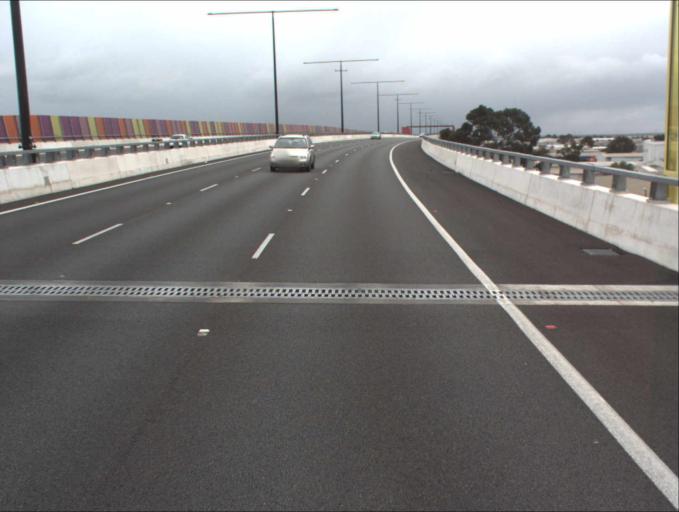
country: AU
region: South Australia
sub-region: Charles Sturt
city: Woodville North
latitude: -34.8570
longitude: 138.5653
